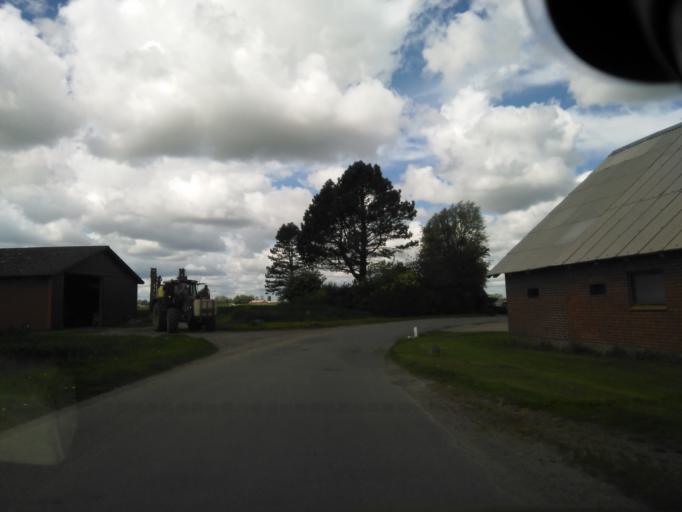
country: DK
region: Central Jutland
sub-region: Arhus Kommune
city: Solbjerg
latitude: 56.0202
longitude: 10.1174
